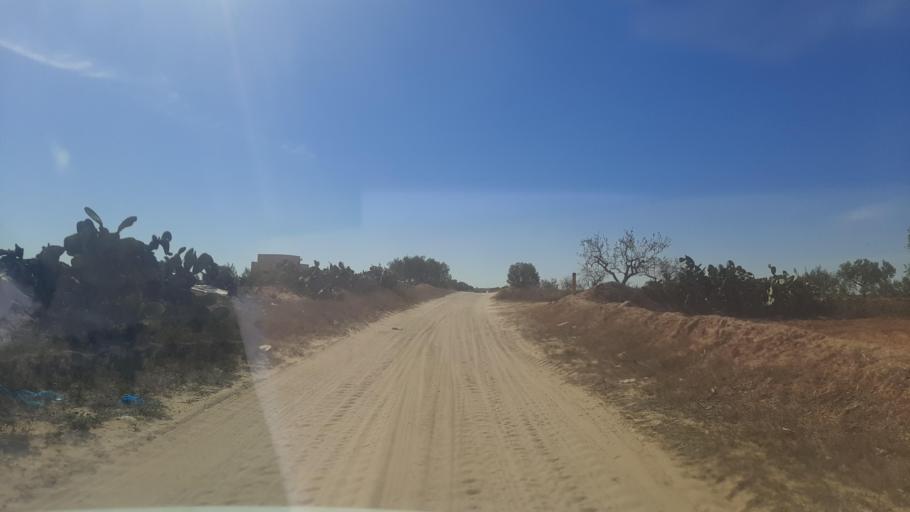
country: TN
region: Safaqis
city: Sfax
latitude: 34.8483
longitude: 10.5618
